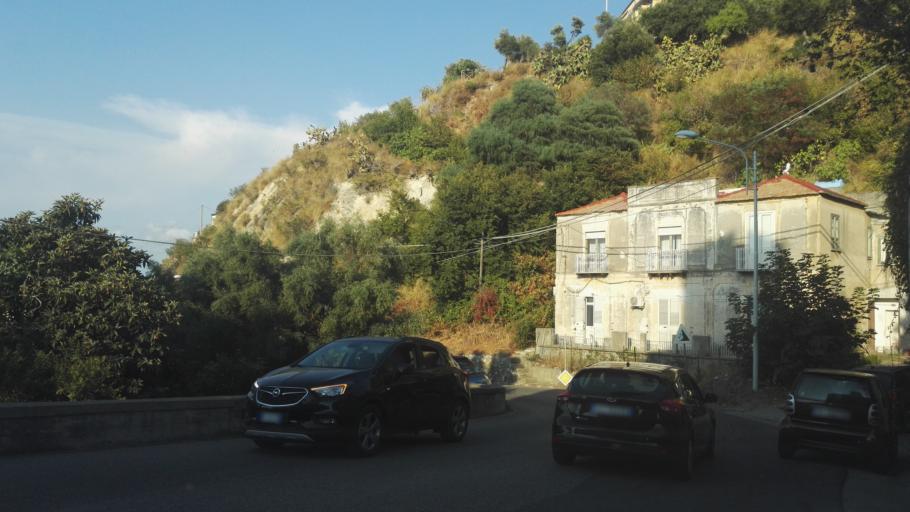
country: IT
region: Calabria
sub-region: Provincia di Vibo-Valentia
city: Pizzo
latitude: 38.7377
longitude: 16.1663
